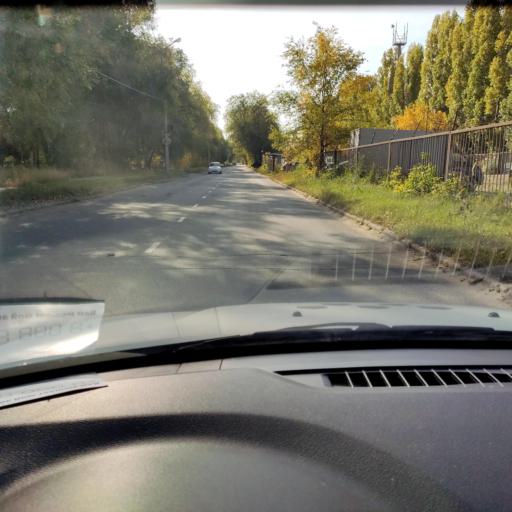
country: RU
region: Samara
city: Tol'yatti
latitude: 53.5544
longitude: 49.3091
